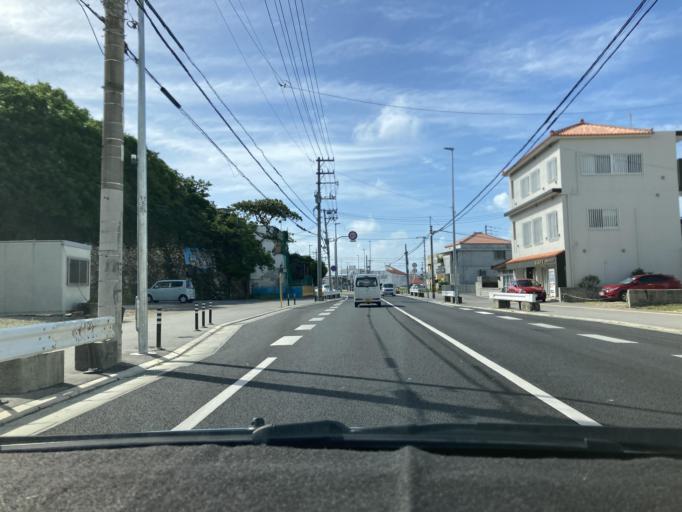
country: JP
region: Okinawa
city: Itoman
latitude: 26.1304
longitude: 127.6699
